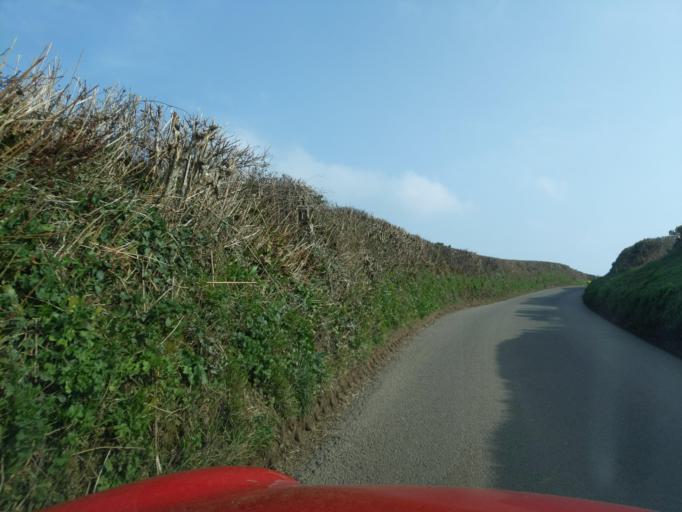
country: GB
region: England
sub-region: Devon
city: Salcombe
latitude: 50.2655
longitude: -3.7199
